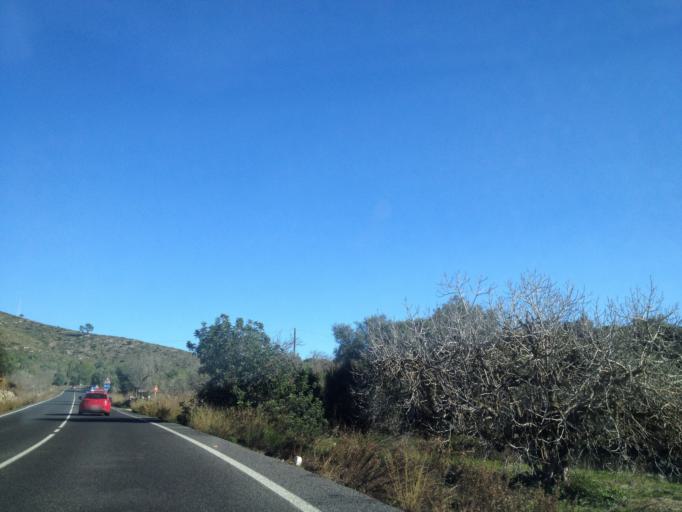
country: ES
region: Balearic Islands
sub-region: Illes Balears
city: Sant Llorenc des Cardassar
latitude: 39.6368
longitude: 3.3048
